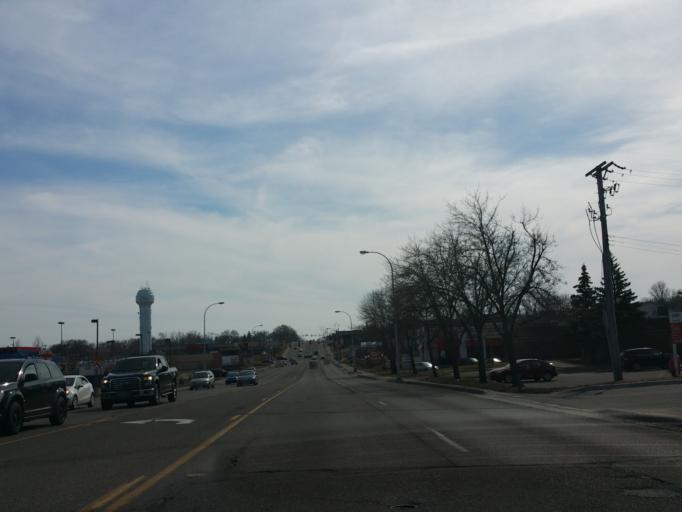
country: US
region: Minnesota
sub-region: Dakota County
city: West Saint Paul
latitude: 44.8977
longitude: -93.0806
